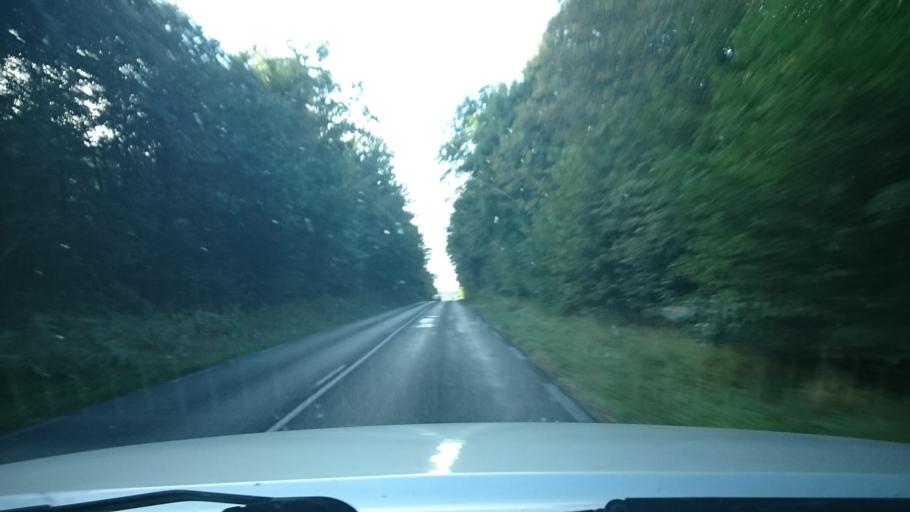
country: FR
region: Ile-de-France
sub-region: Departement de Seine-et-Marne
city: Samoreau
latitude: 48.4098
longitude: 2.7456
